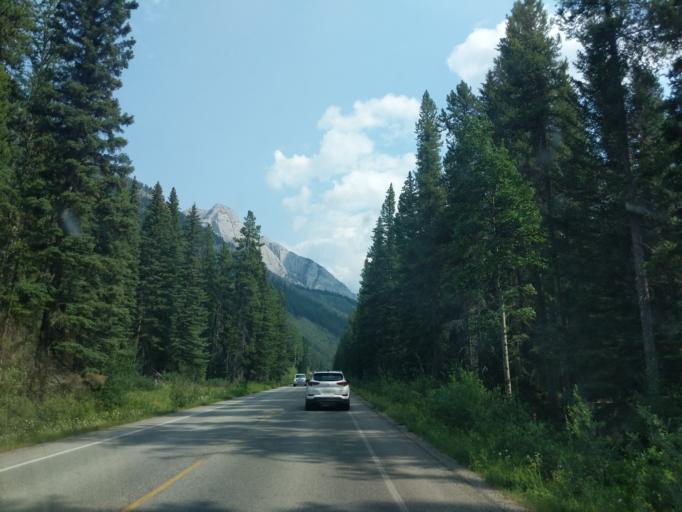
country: CA
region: Alberta
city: Banff
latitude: 51.1925
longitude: -115.7366
